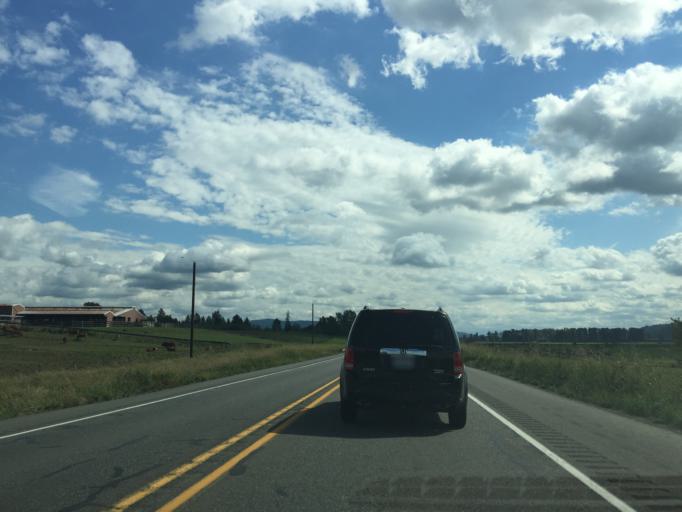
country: US
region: Washington
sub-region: Snohomish County
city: Three Lakes
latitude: 47.8978
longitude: -122.0342
